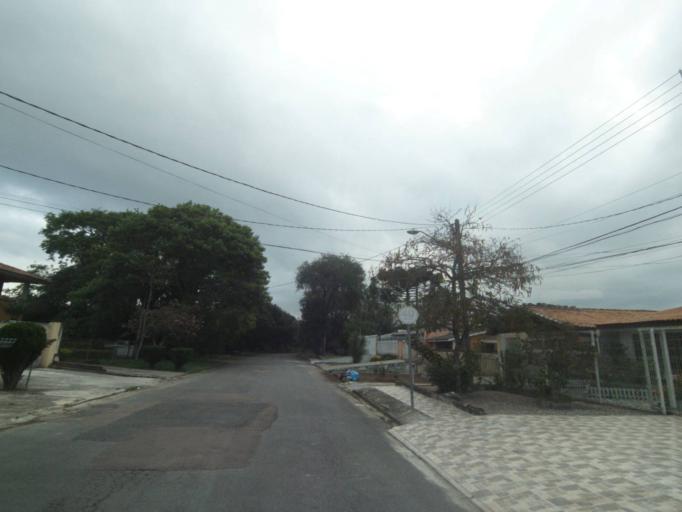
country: BR
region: Parana
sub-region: Pinhais
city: Pinhais
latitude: -25.4175
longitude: -49.2134
